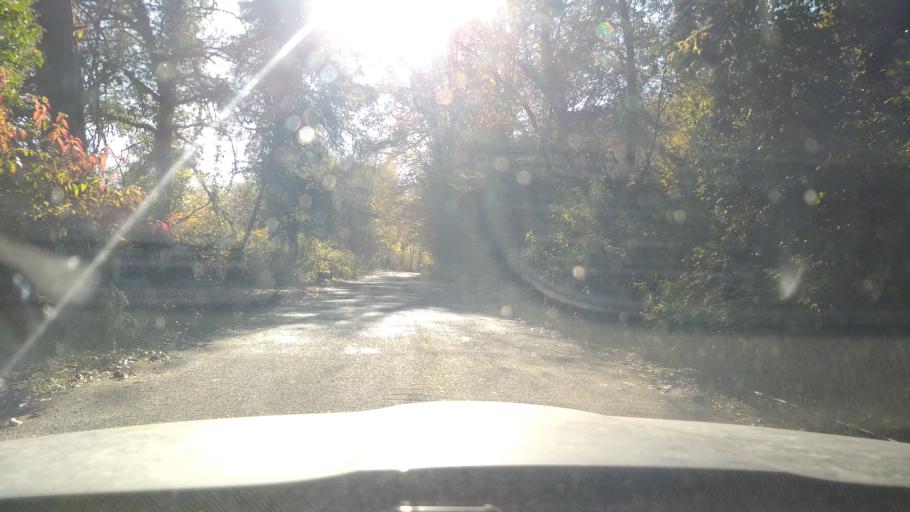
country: GE
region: Abkhazia
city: Bich'vinta
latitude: 43.1842
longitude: 40.4543
